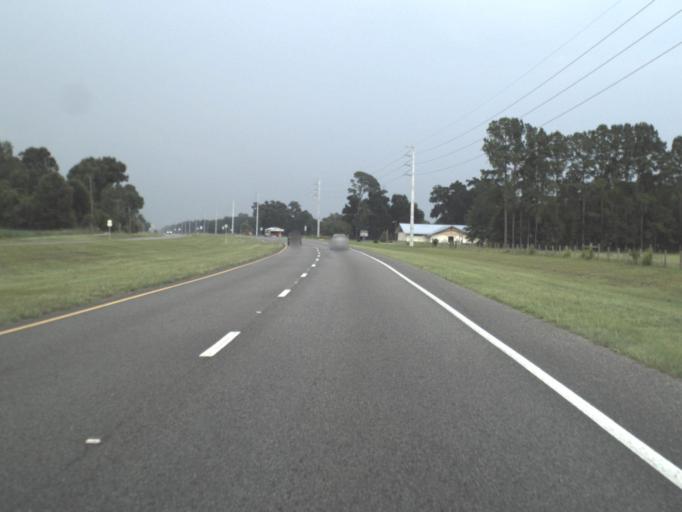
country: US
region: Florida
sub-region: Levy County
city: Chiefland
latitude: 29.4750
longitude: -82.8430
